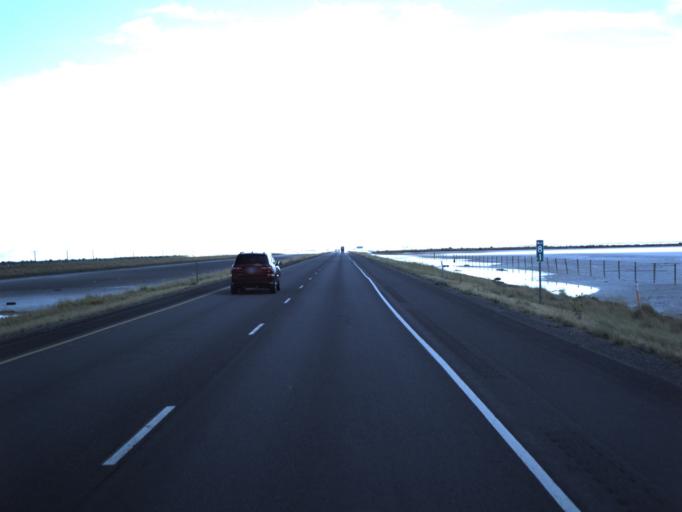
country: US
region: Utah
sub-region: Tooele County
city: Grantsville
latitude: 40.7246
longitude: -112.5708
